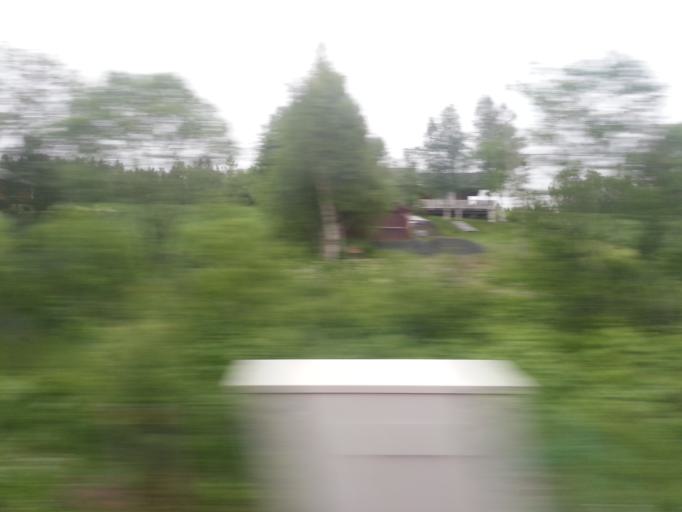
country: NO
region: Sor-Trondelag
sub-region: Rennebu
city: Berkak
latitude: 62.8184
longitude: 10.0196
